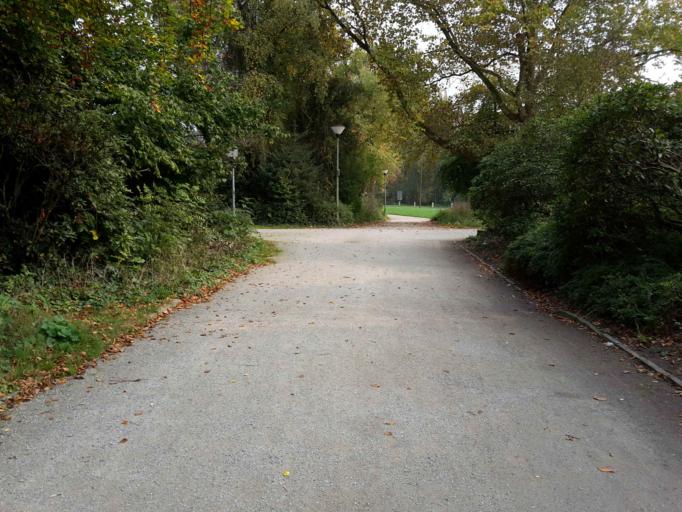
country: DE
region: North Rhine-Westphalia
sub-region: Regierungsbezirk Munster
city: Gelsenkirchen
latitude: 51.5180
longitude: 7.1122
